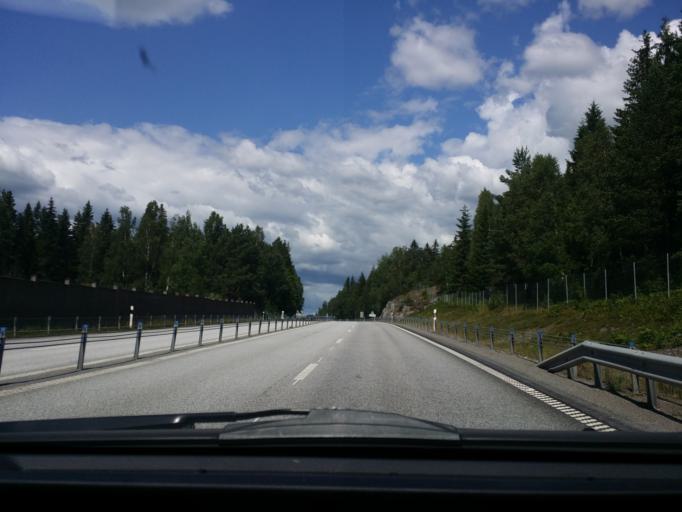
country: SE
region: OErebro
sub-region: Orebro Kommun
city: Hovsta
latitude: 59.3767
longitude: 15.2191
